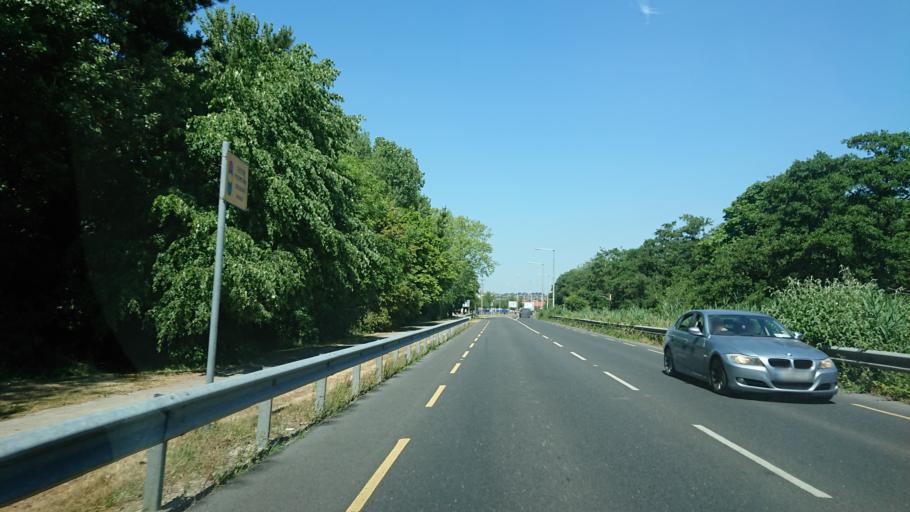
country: IE
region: Munster
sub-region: Waterford
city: Waterford
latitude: 52.2433
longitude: -7.1208
